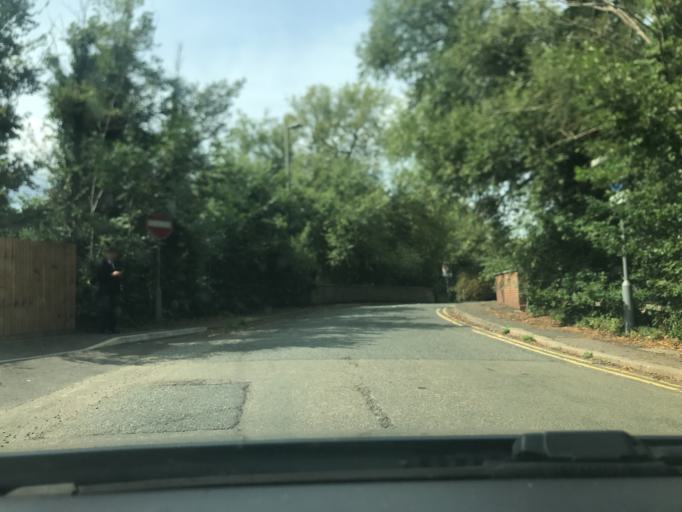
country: GB
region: England
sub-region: Surrey
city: Addlestone
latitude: 51.3731
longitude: -0.4758
